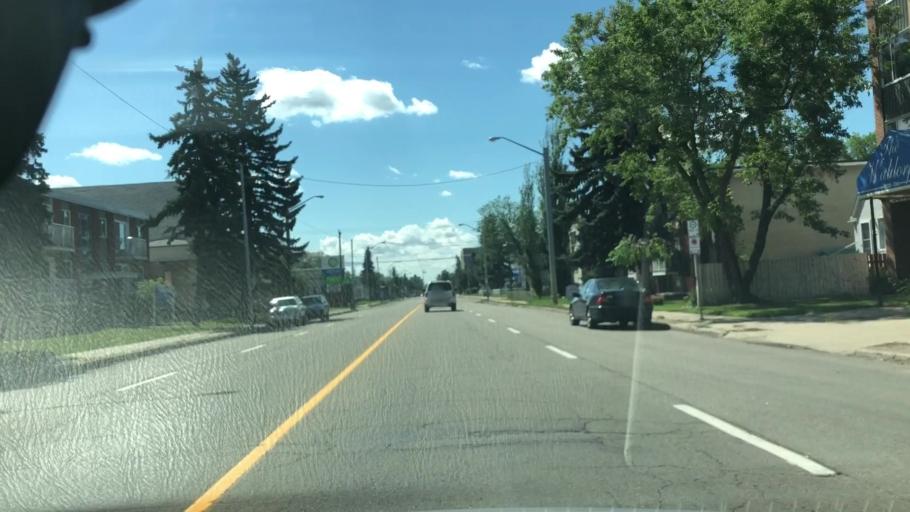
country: CA
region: Alberta
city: Edmonton
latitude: 53.5631
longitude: -113.5360
